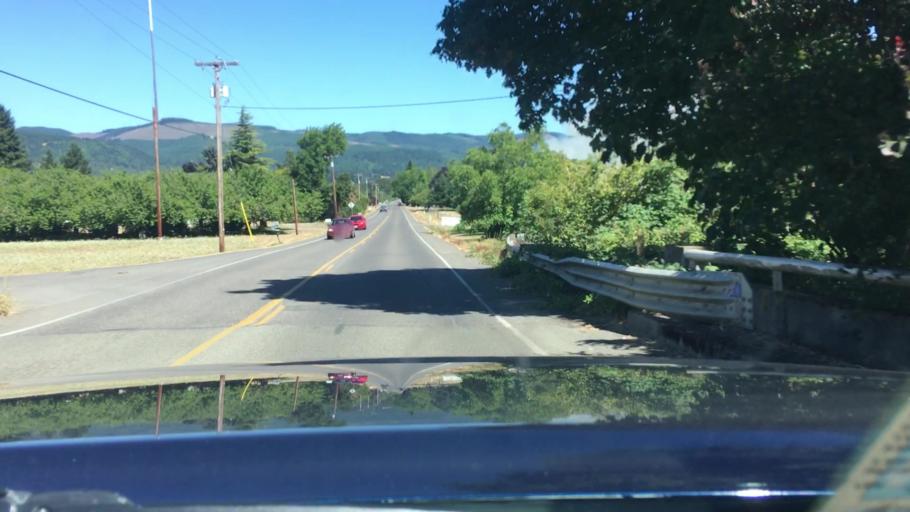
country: US
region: Oregon
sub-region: Lane County
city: Cottage Grove
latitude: 43.8326
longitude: -123.0419
